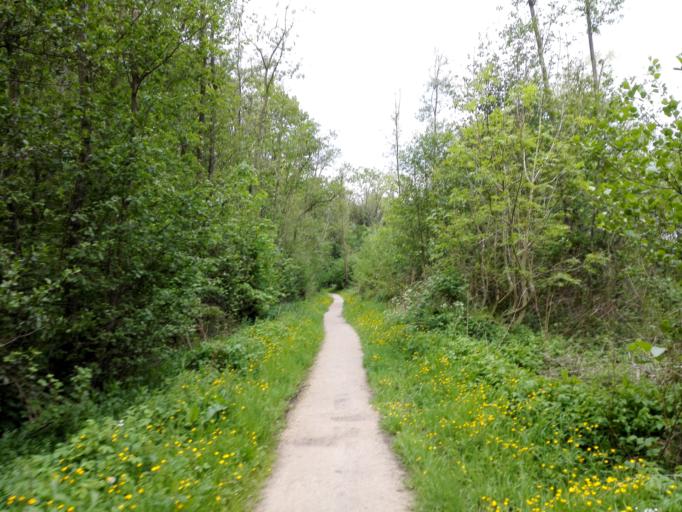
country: BE
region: Flanders
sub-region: Provincie Vlaams-Brabant
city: Huldenberg
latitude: 50.7983
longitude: 4.6026
